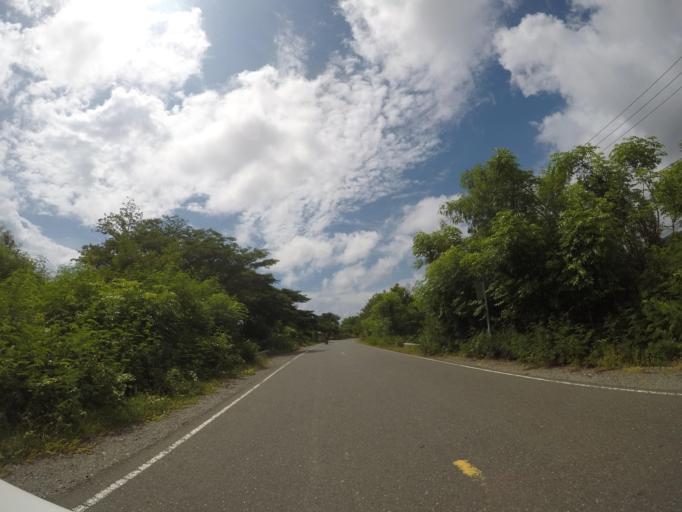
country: TL
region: Liquica
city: Maubara
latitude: -8.7271
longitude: 125.1151
